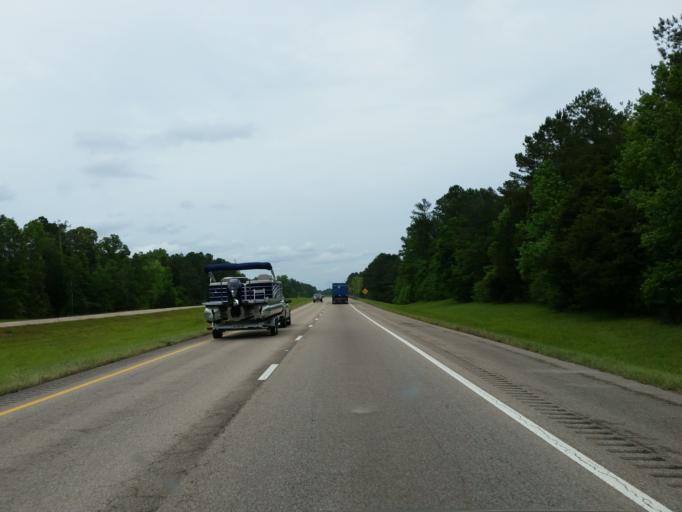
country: US
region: Mississippi
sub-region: Clarke County
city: Stonewall
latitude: 31.9971
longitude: -88.9403
